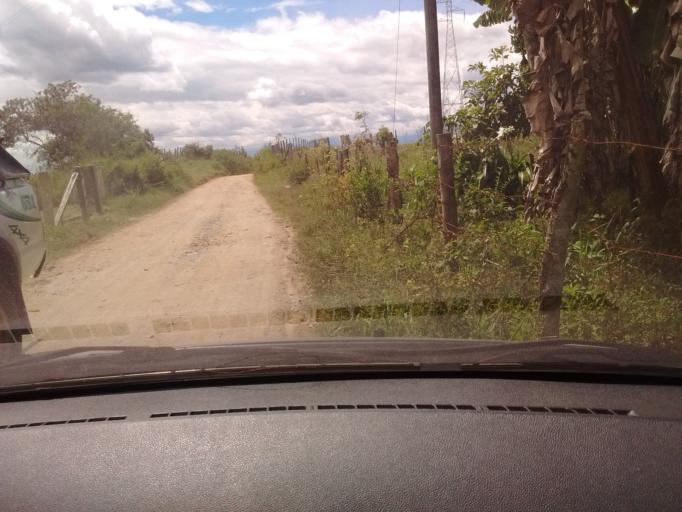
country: CO
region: Cauca
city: El Tambo
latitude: 2.4540
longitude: -76.8267
